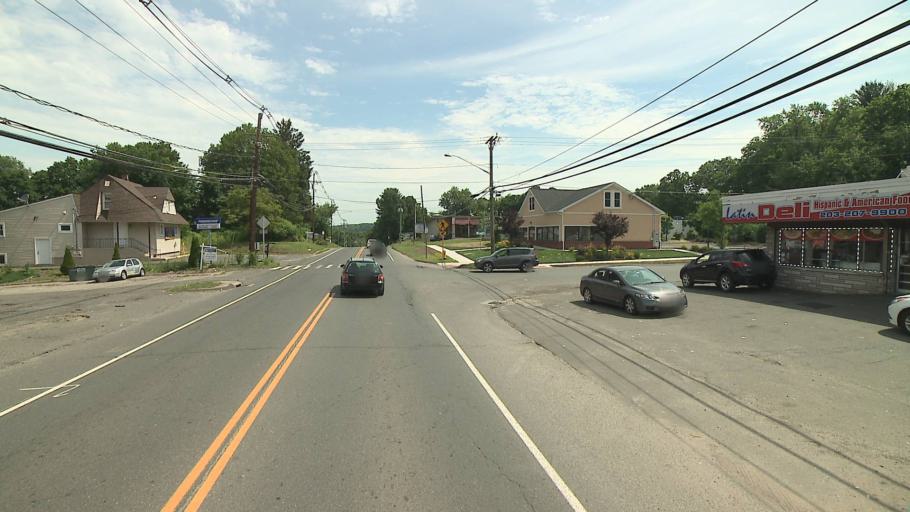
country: US
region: Connecticut
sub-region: Fairfield County
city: Danbury
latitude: 41.4019
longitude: -73.4249
